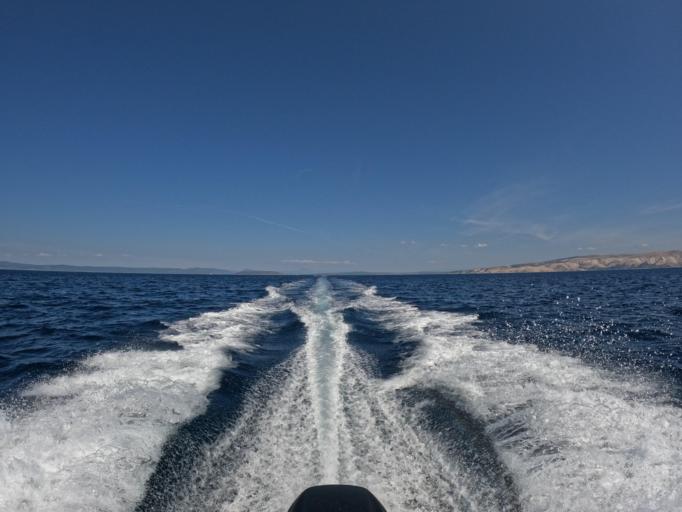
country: HR
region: Primorsko-Goranska
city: Lopar
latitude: 44.8902
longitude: 14.6454
